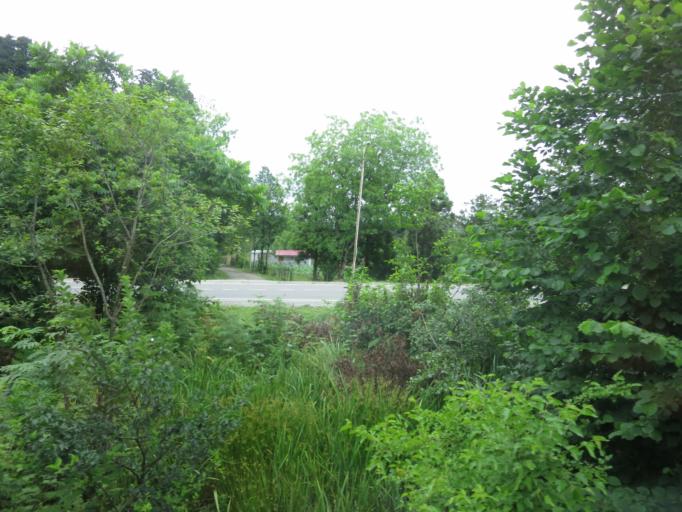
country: GE
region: Guria
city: Urek'i
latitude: 41.9829
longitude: 41.7833
